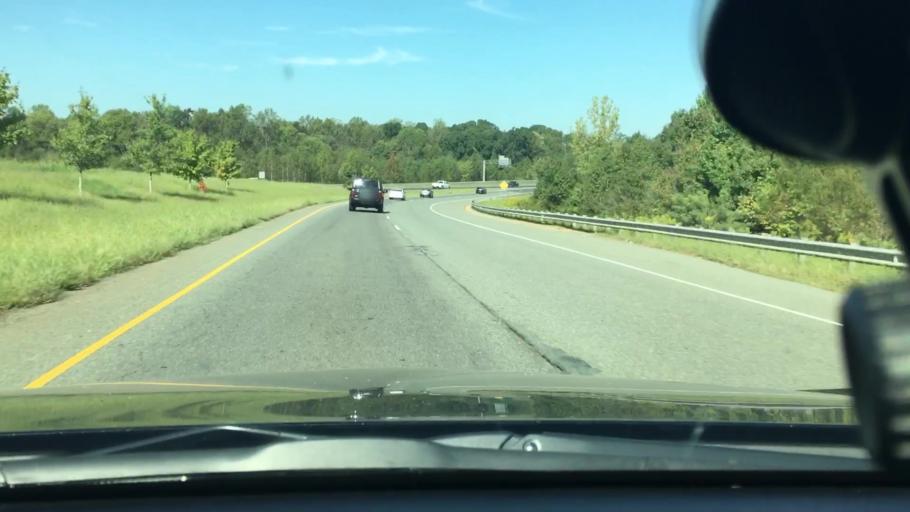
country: US
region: North Carolina
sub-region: Mecklenburg County
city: Mint Hill
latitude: 35.2227
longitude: -80.6497
